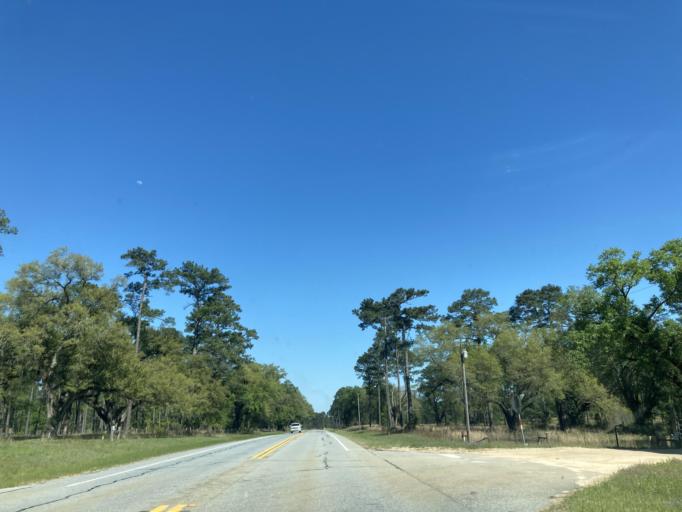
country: US
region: Georgia
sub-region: Baker County
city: Newton
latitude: 31.2134
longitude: -84.4689
